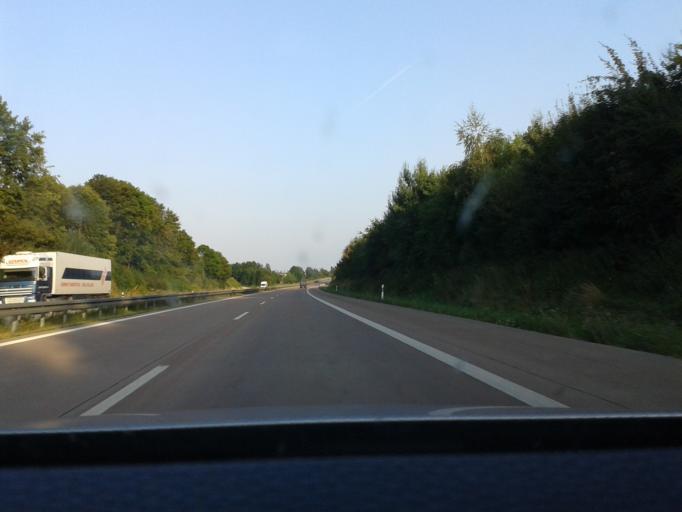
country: DE
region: Saxony
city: Bockelwitz
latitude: 51.2144
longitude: 12.9446
